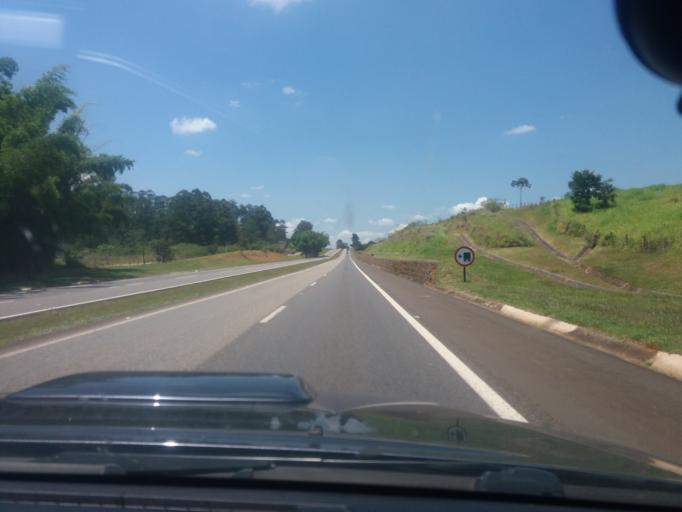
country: BR
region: Sao Paulo
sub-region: Tatui
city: Tatui
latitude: -23.3869
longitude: -47.9236
